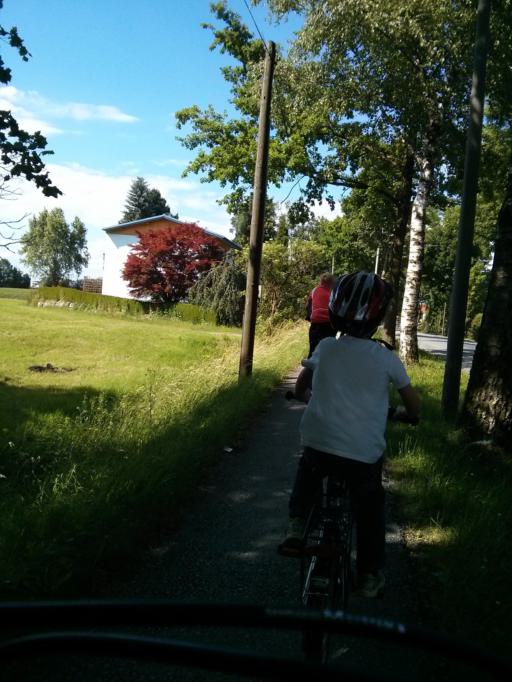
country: AT
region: Salzburg
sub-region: Politischer Bezirk Salzburg-Umgebung
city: Grodig
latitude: 47.7661
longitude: 13.0188
